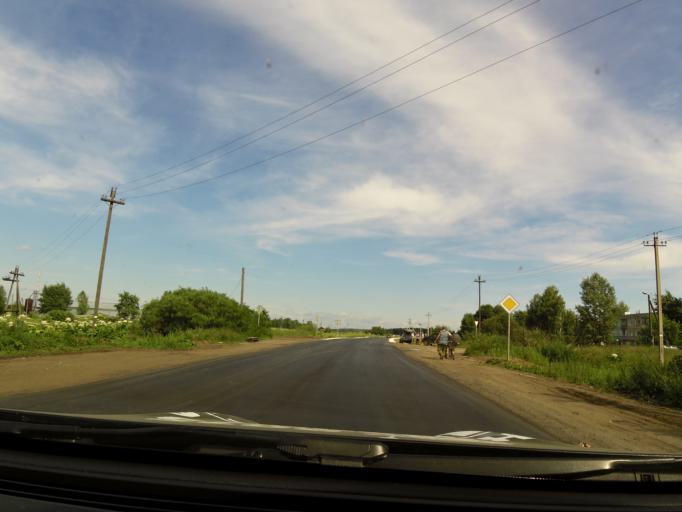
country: RU
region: Kirov
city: Slobodskoy
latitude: 58.7819
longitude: 50.4276
